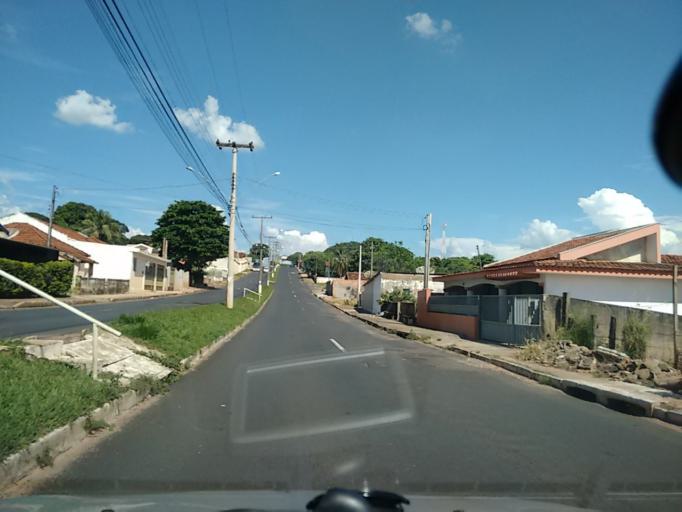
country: BR
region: Sao Paulo
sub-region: Pompeia
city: Pompeia
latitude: -22.0979
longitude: -50.2533
